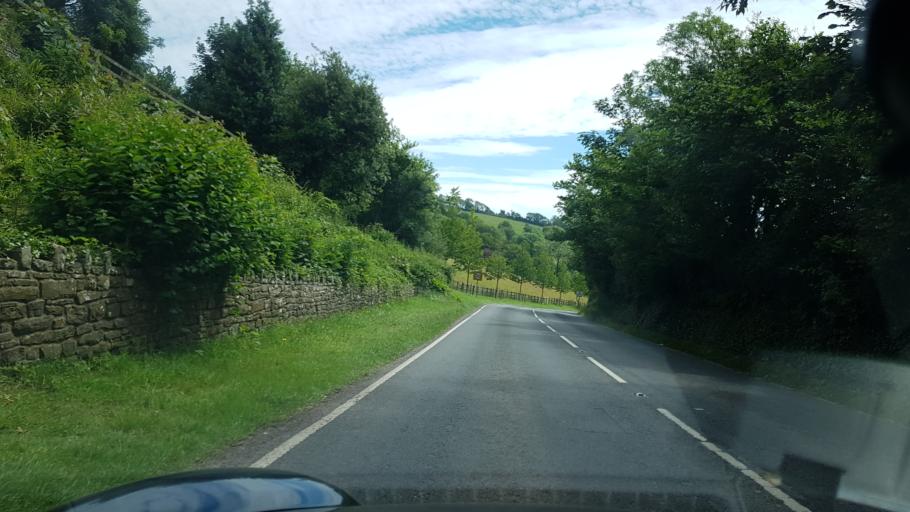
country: GB
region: Wales
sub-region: Carmarthenshire
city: Saint Clears
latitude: 51.7769
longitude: -4.4663
